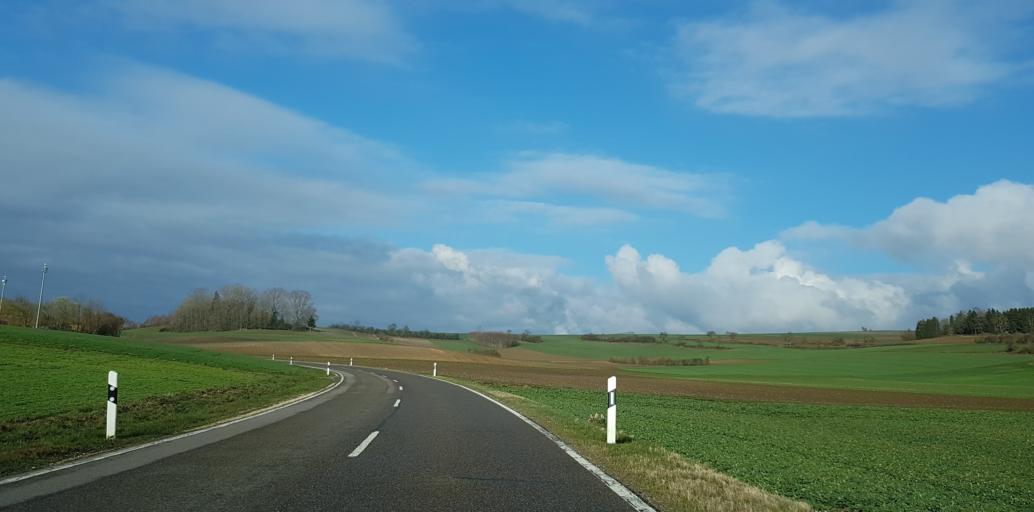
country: DE
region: Baden-Wuerttemberg
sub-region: Tuebingen Region
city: Altheim
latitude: 48.3314
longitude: 9.7960
